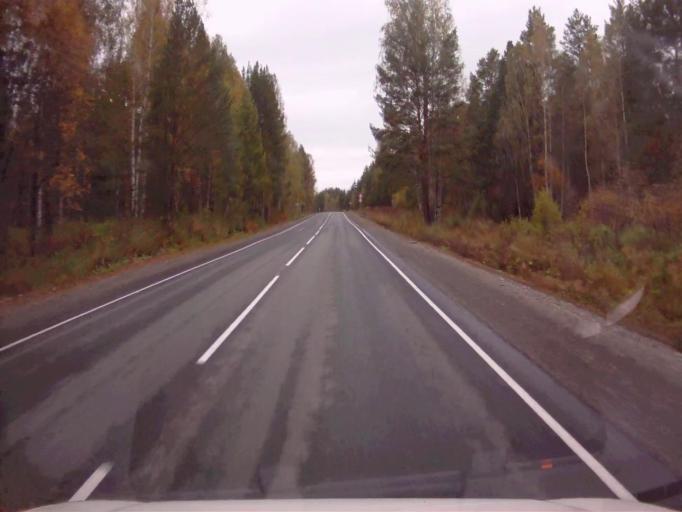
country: RU
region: Chelyabinsk
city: Nyazepetrovsk
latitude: 56.0584
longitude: 59.7332
